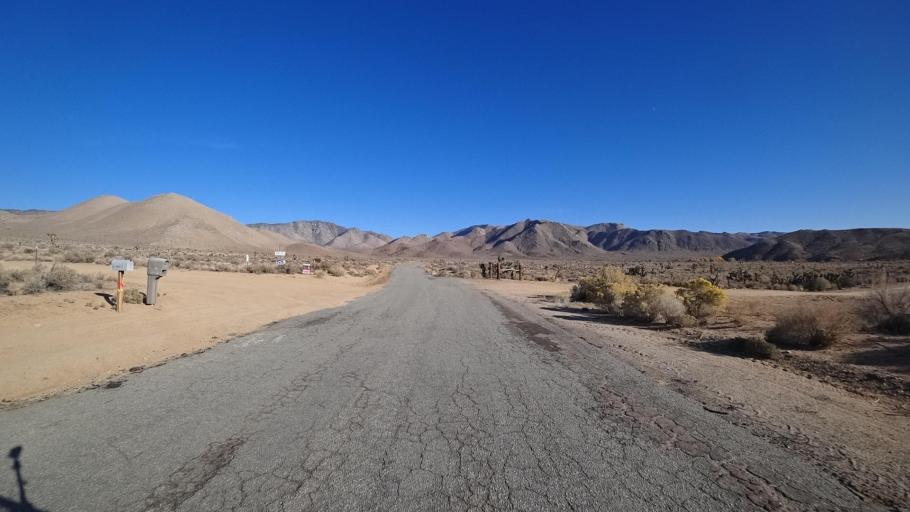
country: US
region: California
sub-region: Kern County
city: Weldon
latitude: 35.5554
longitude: -118.2197
